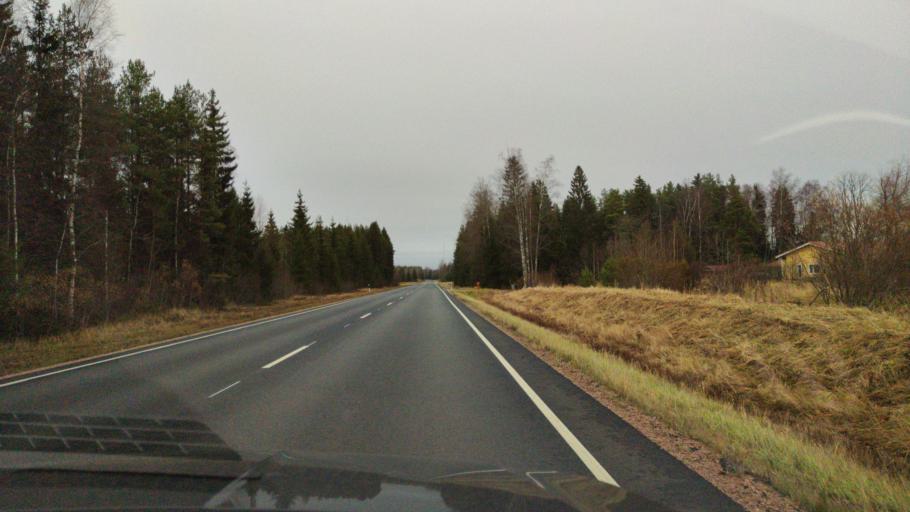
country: FI
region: Varsinais-Suomi
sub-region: Loimaa
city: Aura
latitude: 60.7076
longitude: 22.4426
